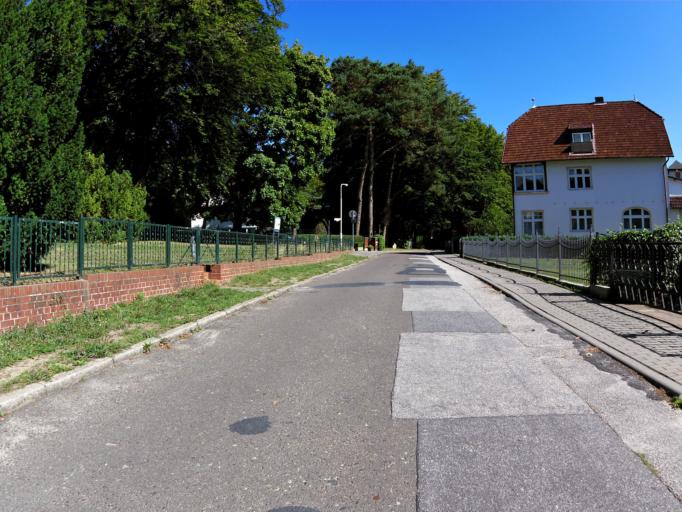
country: DE
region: Mecklenburg-Vorpommern
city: Seebad Bansin
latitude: 53.9717
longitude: 14.1392
